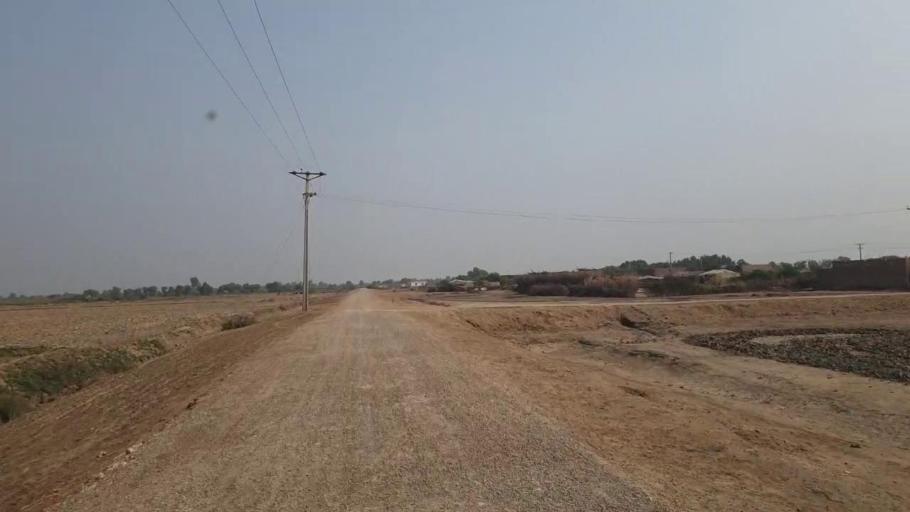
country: PK
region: Sindh
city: Kario
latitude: 24.9082
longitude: 68.5929
